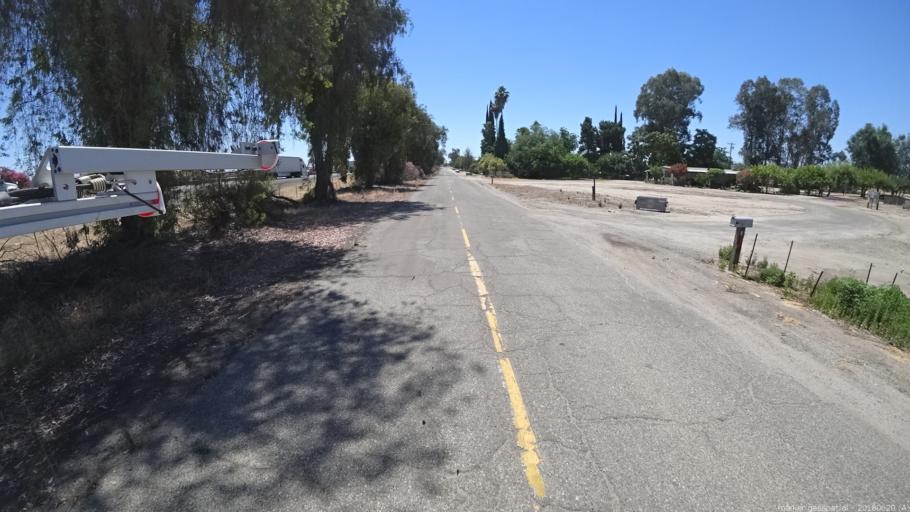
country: US
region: California
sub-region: Madera County
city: Parksdale
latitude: 36.8909
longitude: -119.9875
